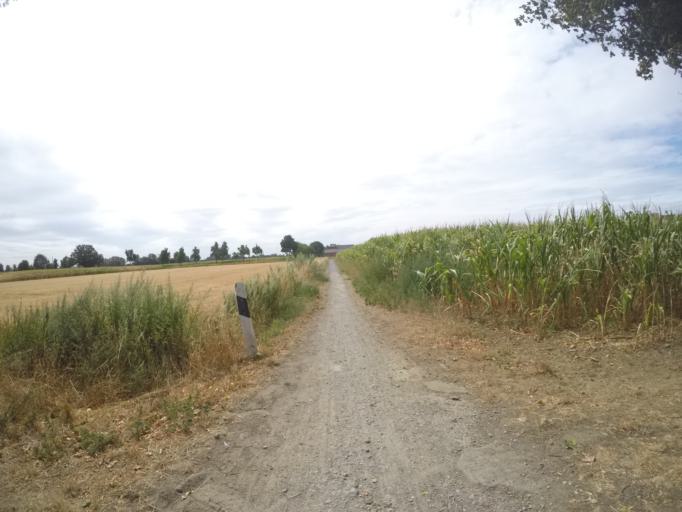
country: DE
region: North Rhine-Westphalia
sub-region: Regierungsbezirk Dusseldorf
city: Bocholt
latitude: 51.8552
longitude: 6.5591
